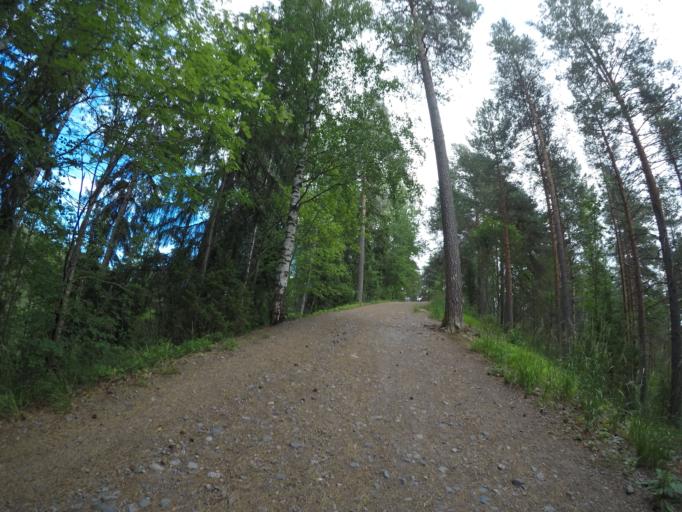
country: FI
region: Haeme
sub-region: Haemeenlinna
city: Haemeenlinna
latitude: 60.9983
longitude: 24.4172
